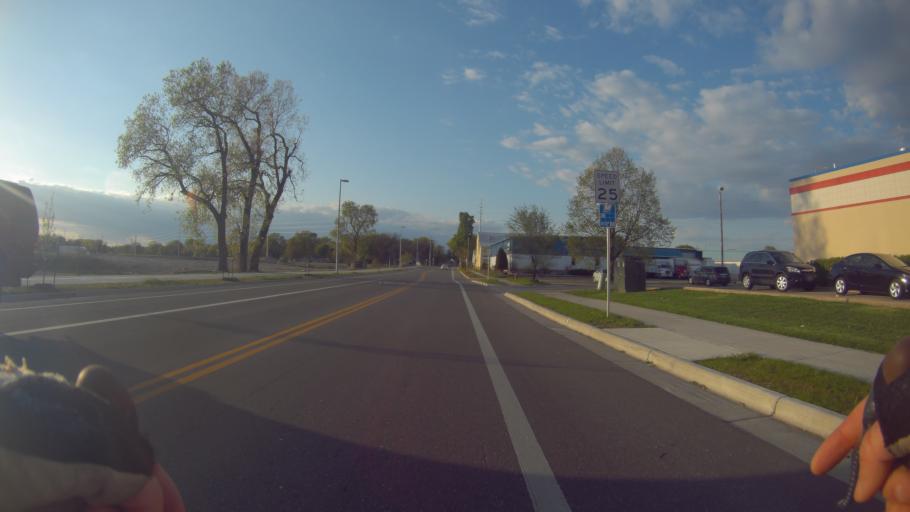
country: US
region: Wisconsin
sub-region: Dane County
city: Monona
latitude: 43.0841
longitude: -89.3162
